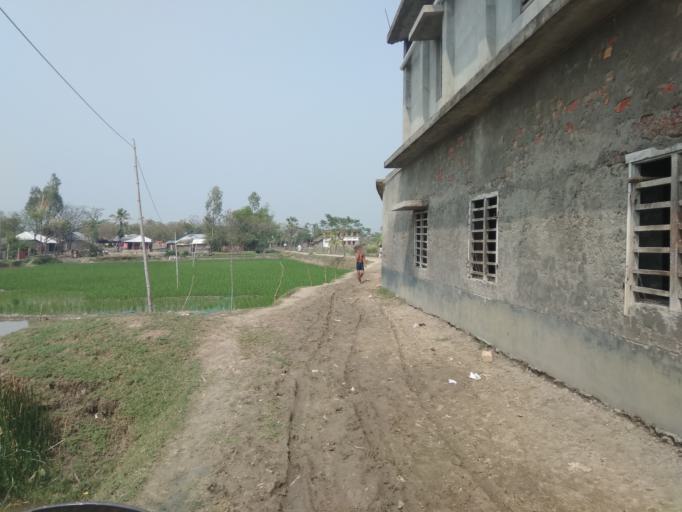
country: IN
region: West Bengal
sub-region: North 24 Parganas
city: Taki
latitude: 22.3490
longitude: 89.2200
